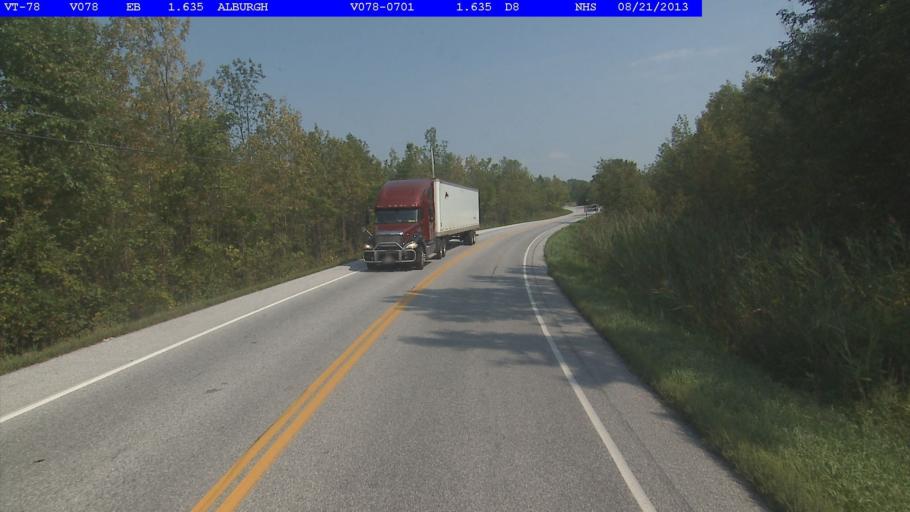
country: US
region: New York
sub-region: Clinton County
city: Rouses Point
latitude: 44.9723
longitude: -73.2512
